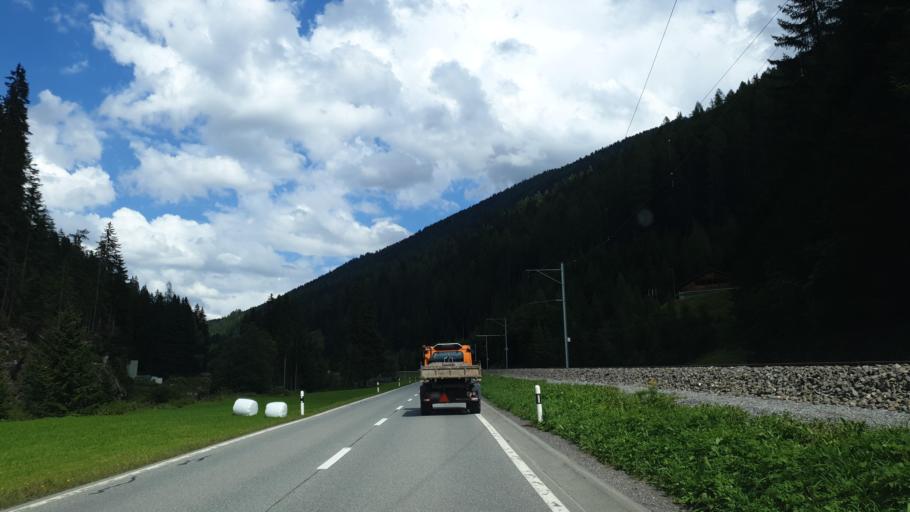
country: CH
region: Grisons
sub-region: Plessur District
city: Arosa
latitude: 46.7183
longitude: 9.7629
